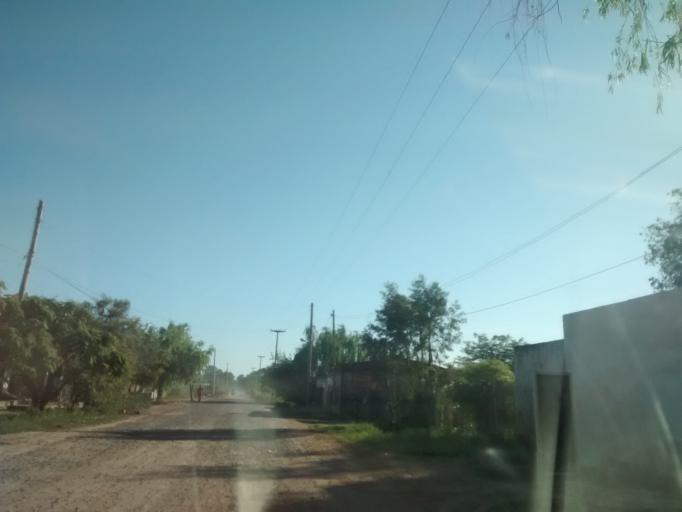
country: AR
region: Chaco
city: Resistencia
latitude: -27.4641
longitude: -58.9649
